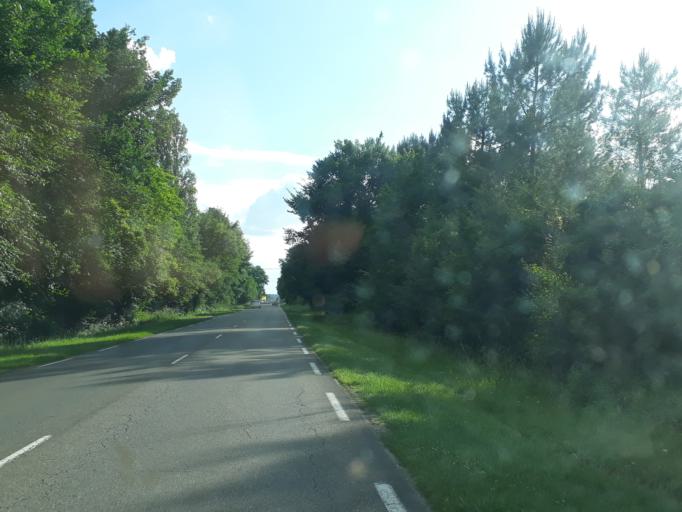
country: FR
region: Aquitaine
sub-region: Departement des Landes
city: Mont-de-Marsan
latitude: 43.9151
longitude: -0.4567
